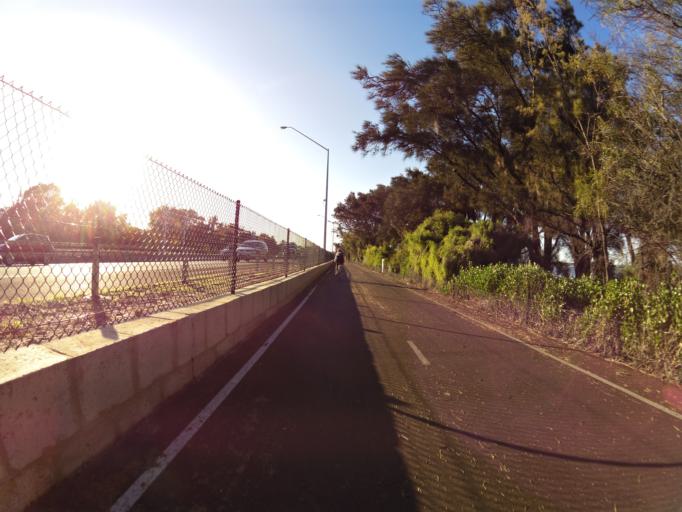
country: AU
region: Western Australia
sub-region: South Perth
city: Como
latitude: -31.9805
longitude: 115.8486
